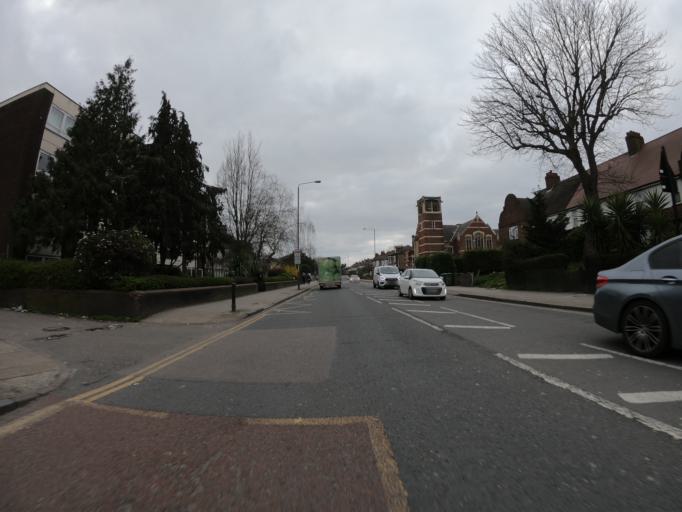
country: GB
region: England
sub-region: Greater London
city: Blackheath
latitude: 51.4748
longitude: 0.0339
